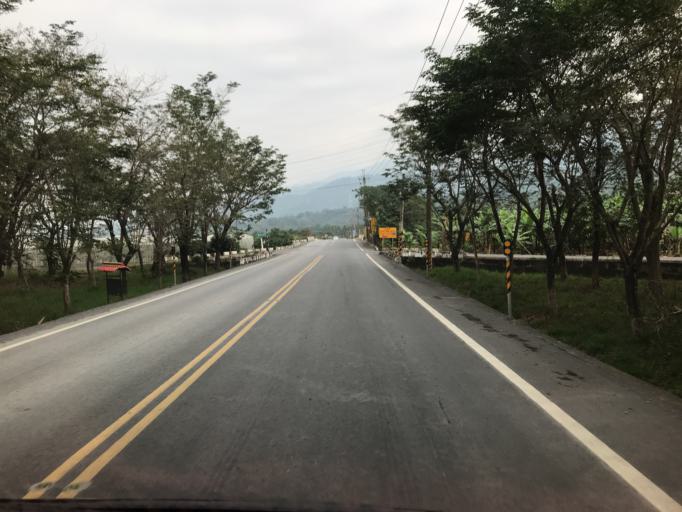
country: TW
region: Taiwan
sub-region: Pingtung
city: Pingtung
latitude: 22.4539
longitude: 120.6115
